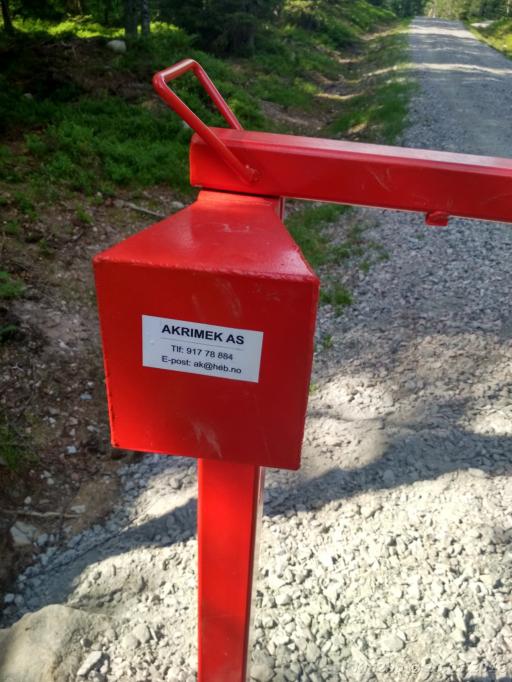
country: NO
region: Akershus
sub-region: Nannestad
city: Maura
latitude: 60.3020
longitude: 10.9804
